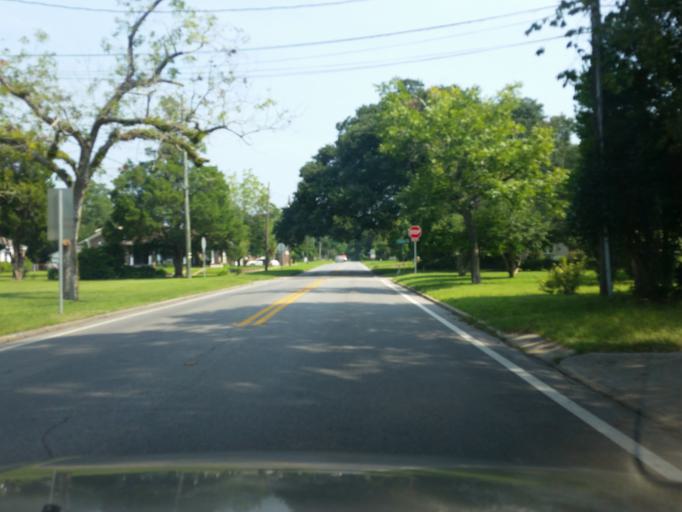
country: US
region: Florida
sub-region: Escambia County
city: East Pensacola Heights
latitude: 30.4349
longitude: -87.1975
